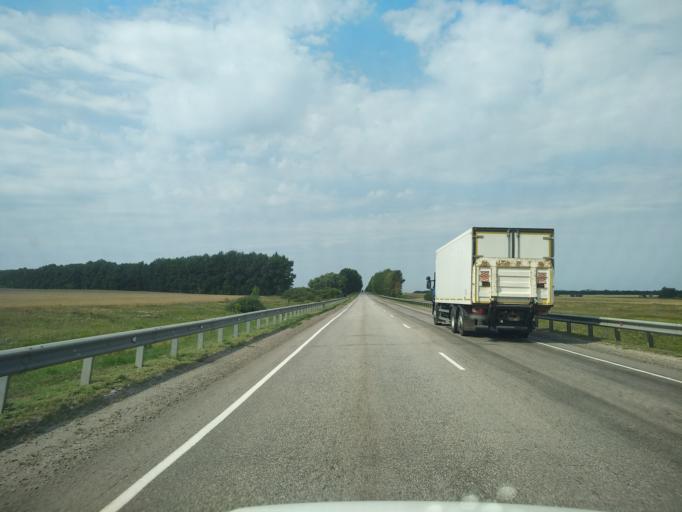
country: RU
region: Voronezj
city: Pereleshino
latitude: 51.7322
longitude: 40.0640
